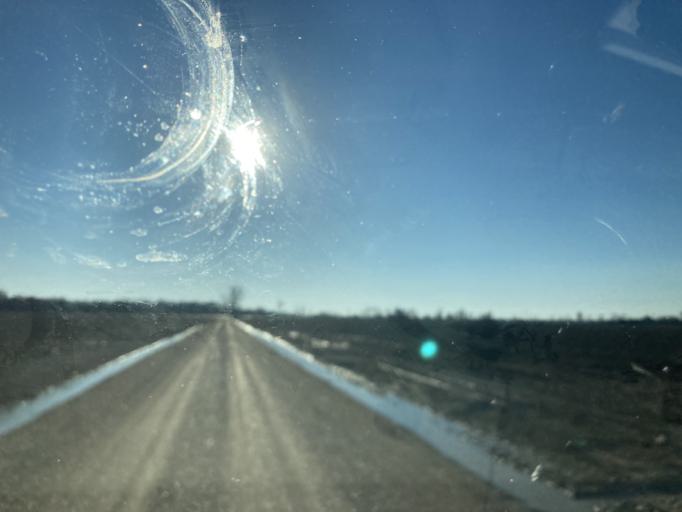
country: US
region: Mississippi
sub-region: Yazoo County
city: Yazoo City
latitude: 32.9242
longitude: -90.6121
